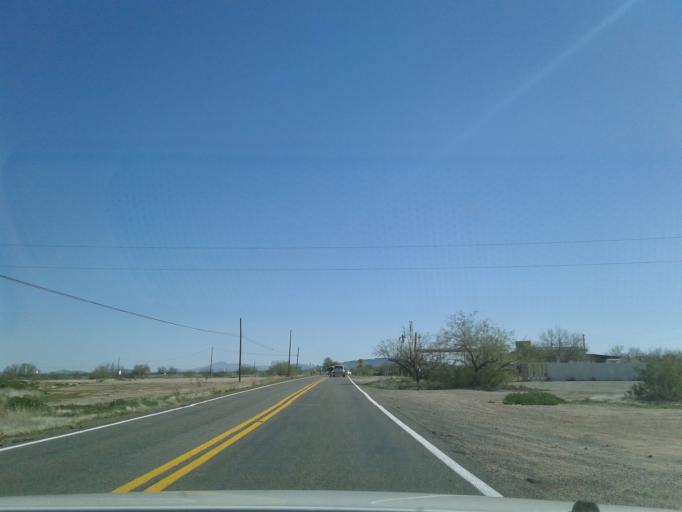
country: US
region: Arizona
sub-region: Pima County
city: Avra Valley
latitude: 32.5735
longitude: -111.3279
